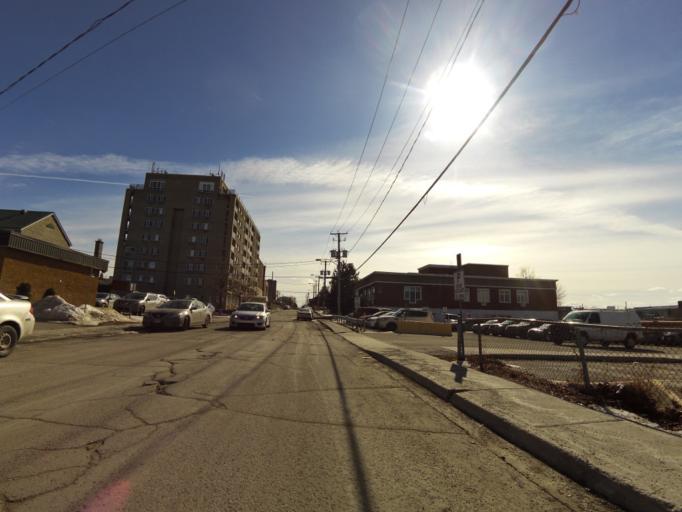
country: CA
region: Ontario
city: Ottawa
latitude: 45.4342
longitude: -75.7237
